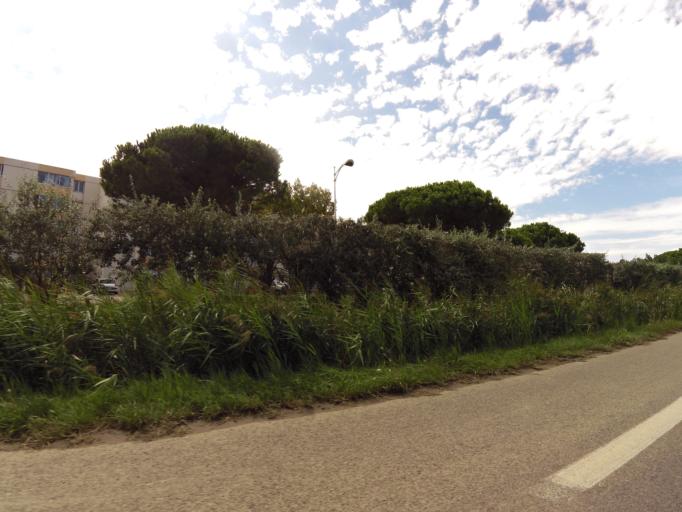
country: FR
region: Languedoc-Roussillon
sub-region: Departement du Gard
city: Le Grau-du-Roi
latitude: 43.5326
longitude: 4.1477
